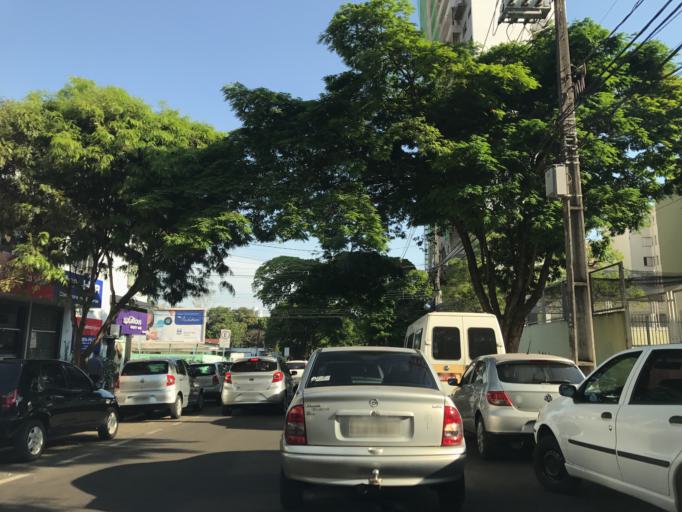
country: BR
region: Parana
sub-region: Maringa
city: Maringa
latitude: -23.4216
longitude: -51.9309
